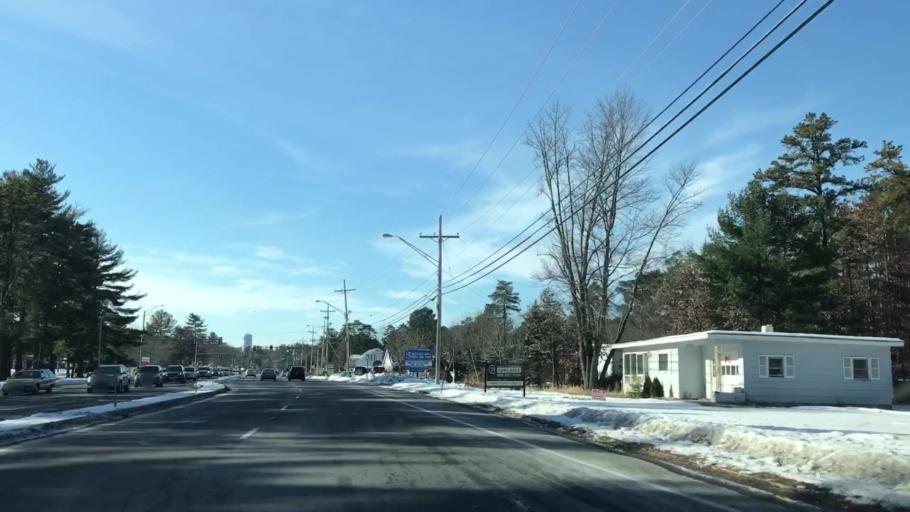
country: US
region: New Hampshire
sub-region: Hillsborough County
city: Hollis
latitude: 42.8116
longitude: -71.5808
